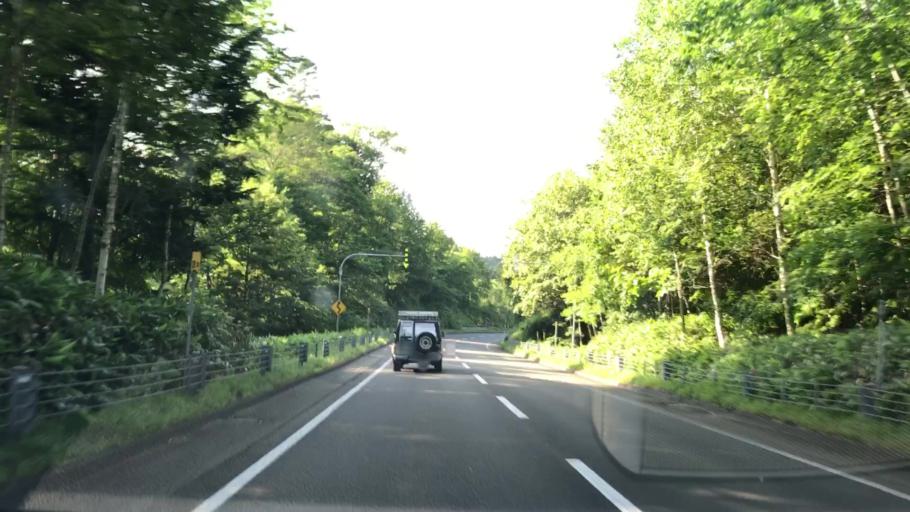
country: JP
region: Hokkaido
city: Iwamizawa
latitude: 42.9045
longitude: 142.1271
